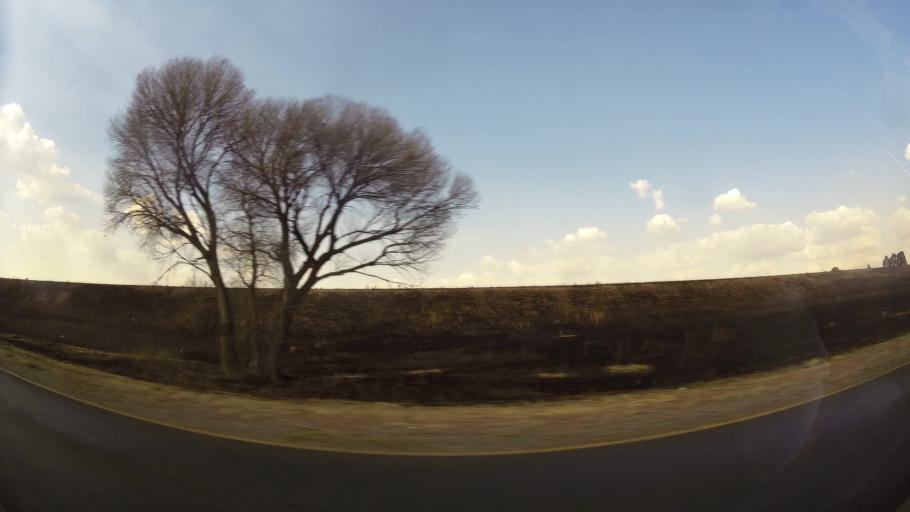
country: ZA
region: Gauteng
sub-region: Ekurhuleni Metropolitan Municipality
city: Springs
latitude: -26.3650
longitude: 28.3413
